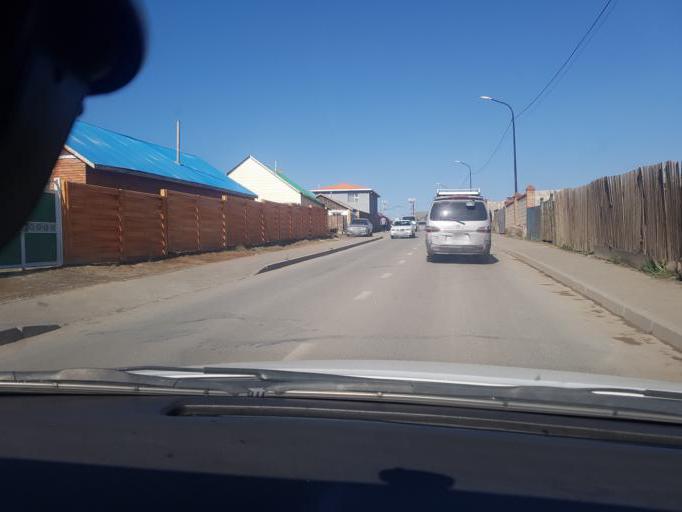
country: MN
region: Ulaanbaatar
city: Ulaanbaatar
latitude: 47.9492
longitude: 106.8666
